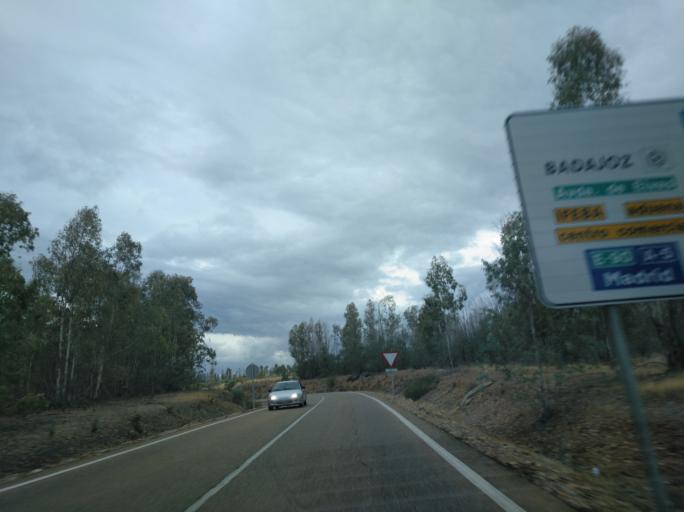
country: ES
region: Extremadura
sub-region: Provincia de Badajoz
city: Badajoz
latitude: 38.8865
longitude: -7.0246
